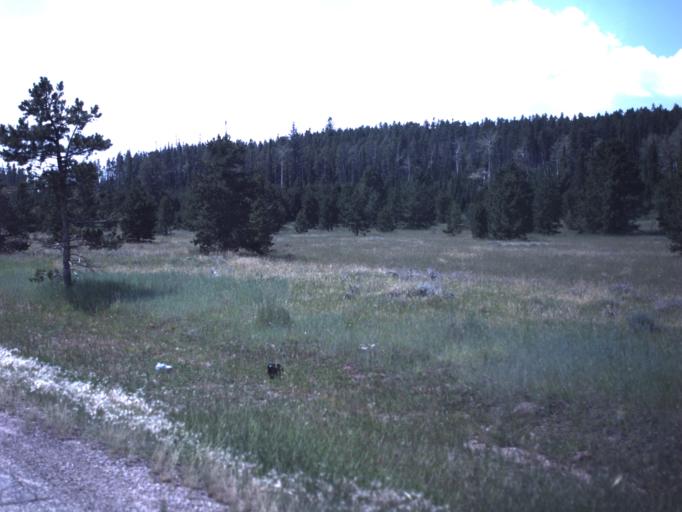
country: US
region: Utah
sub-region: Daggett County
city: Manila
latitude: 40.8003
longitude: -109.4666
